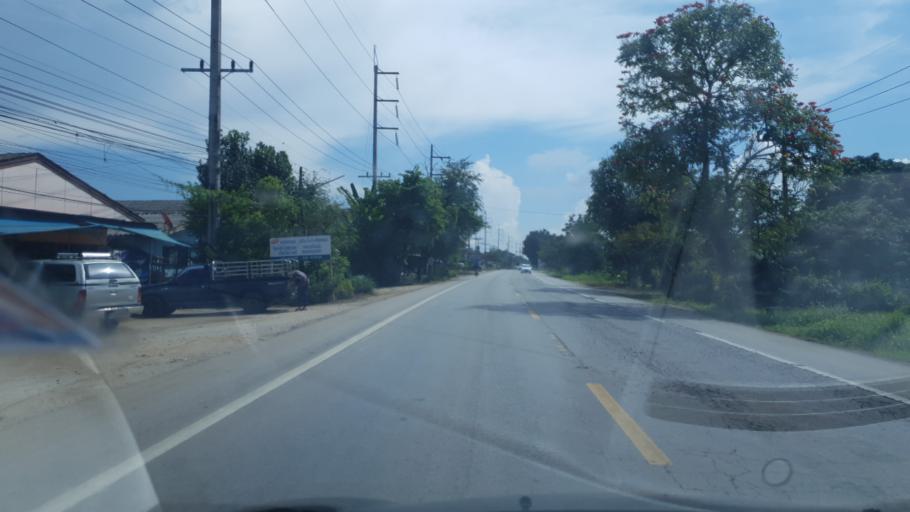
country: TH
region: Chiang Rai
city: Wiang Pa Pao
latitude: 19.3877
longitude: 99.5027
